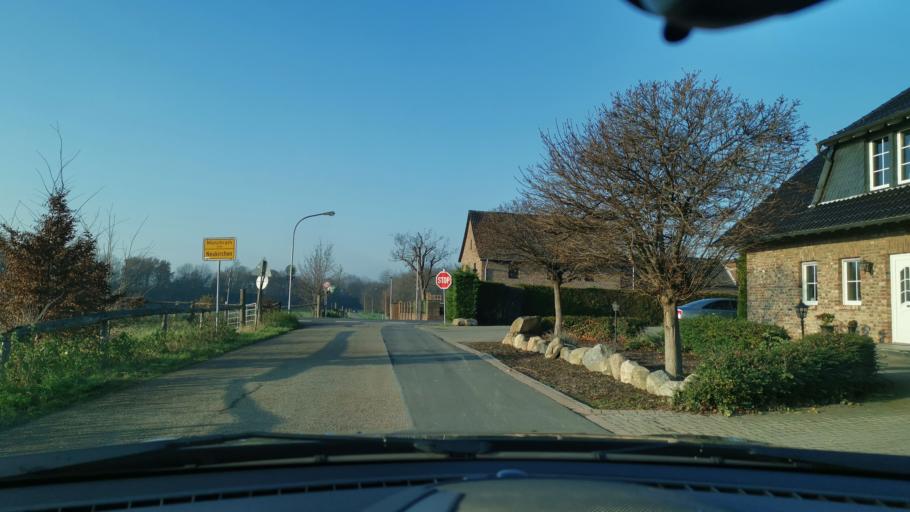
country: DE
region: North Rhine-Westphalia
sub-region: Regierungsbezirk Dusseldorf
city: Neubrueck
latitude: 51.1271
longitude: 6.6740
